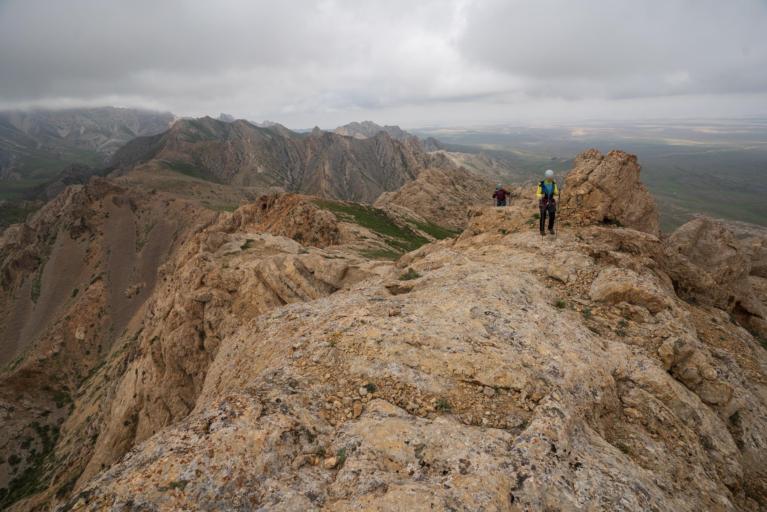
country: KZ
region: Ongtustik Qazaqstan
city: Ashchysay
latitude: 43.7449
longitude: 68.8354
